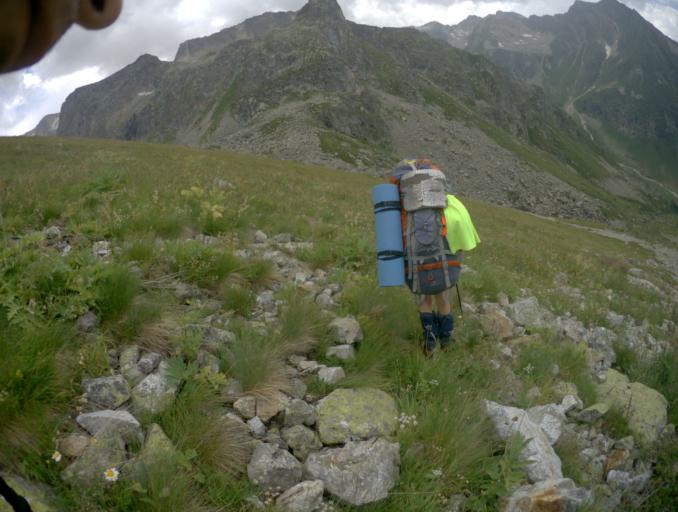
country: RU
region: Karachayevo-Cherkesiya
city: Uchkulan
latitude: 43.2919
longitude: 42.0793
